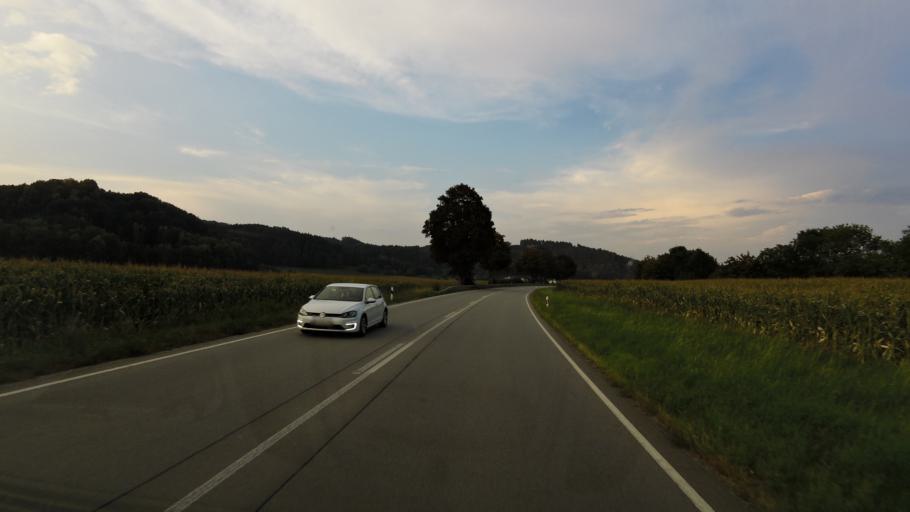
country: DE
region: Bavaria
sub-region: Lower Bavaria
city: Stubenberg
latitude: 48.2914
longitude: 13.0938
